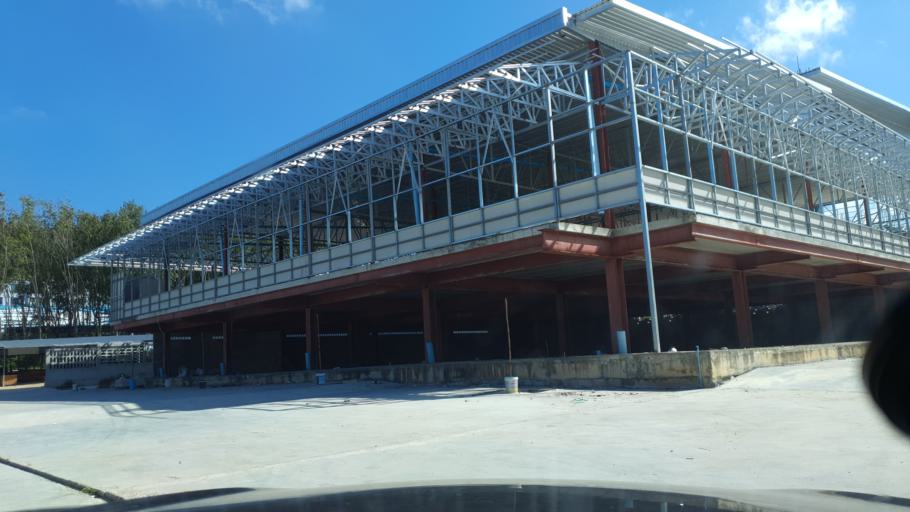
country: TH
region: Phangnga
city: Ban Ao Nang
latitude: 8.0550
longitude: 98.8163
